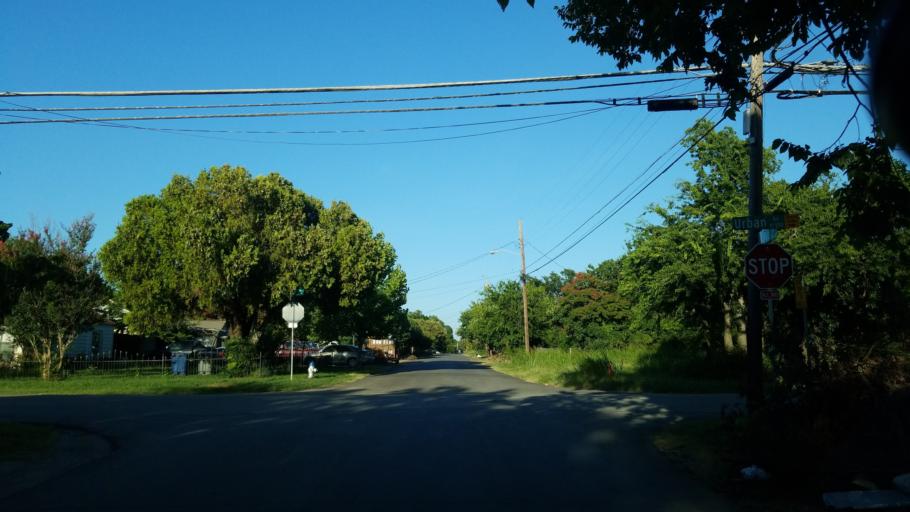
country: US
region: Texas
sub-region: Dallas County
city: Balch Springs
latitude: 32.7770
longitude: -96.6967
